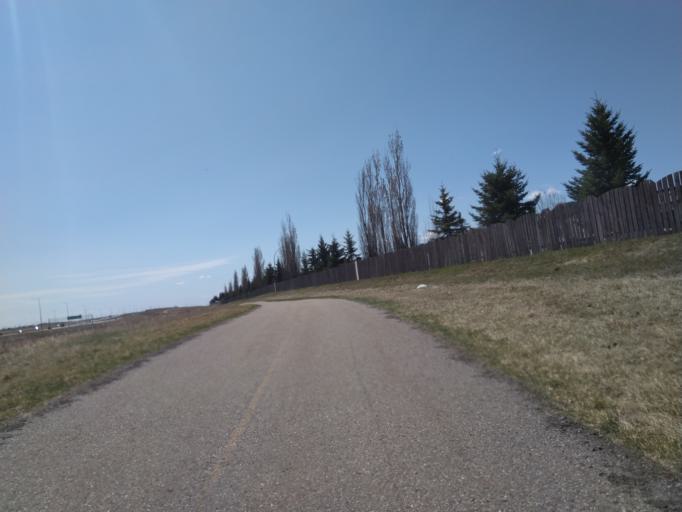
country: CA
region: Alberta
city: Chestermere
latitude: 51.0808
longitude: -113.9228
